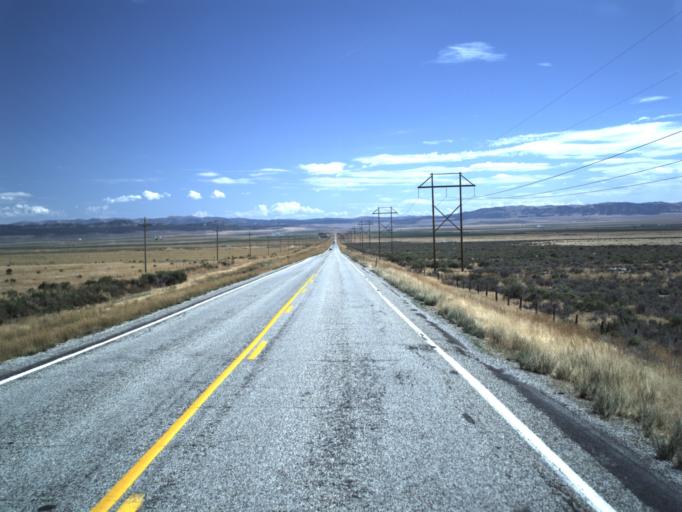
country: US
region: Idaho
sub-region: Oneida County
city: Malad City
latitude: 41.9658
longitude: -112.9927
